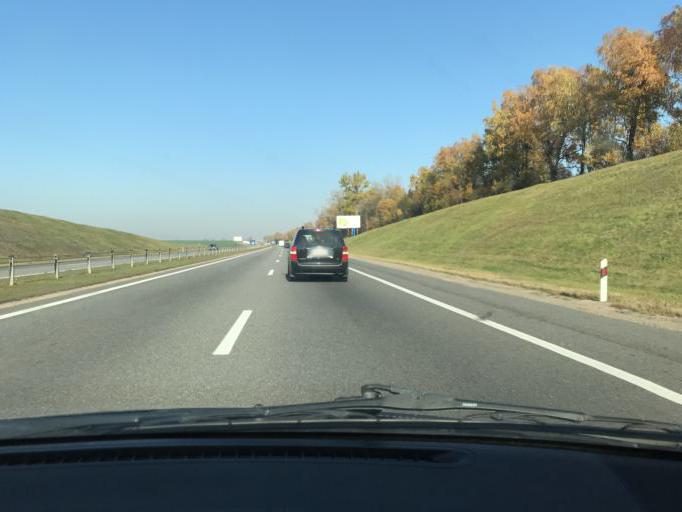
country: BY
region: Minsk
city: Samakhvalavichy
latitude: 53.7683
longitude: 27.5217
